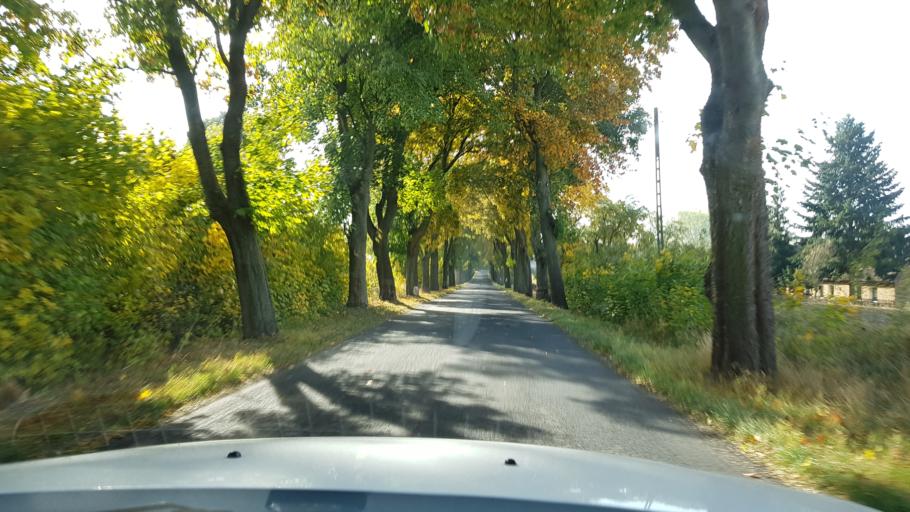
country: PL
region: West Pomeranian Voivodeship
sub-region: Powiat mysliborski
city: Nowogrodek Pomorski
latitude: 52.9463
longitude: 15.0961
